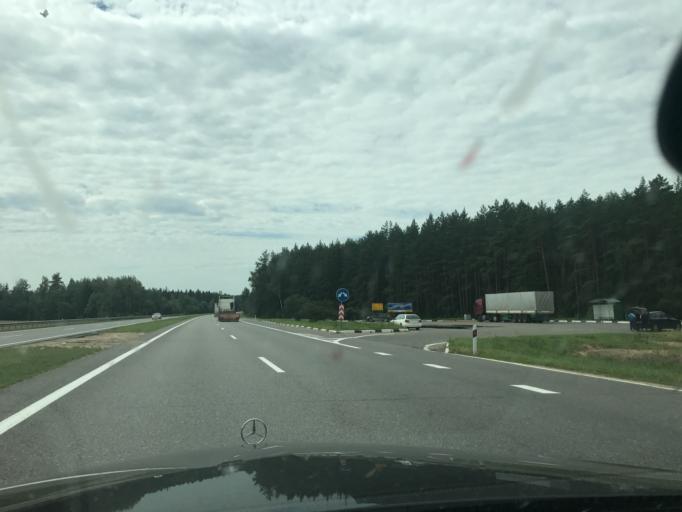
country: BY
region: Minsk
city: Zamostochcha
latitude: 53.8767
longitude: 27.9304
